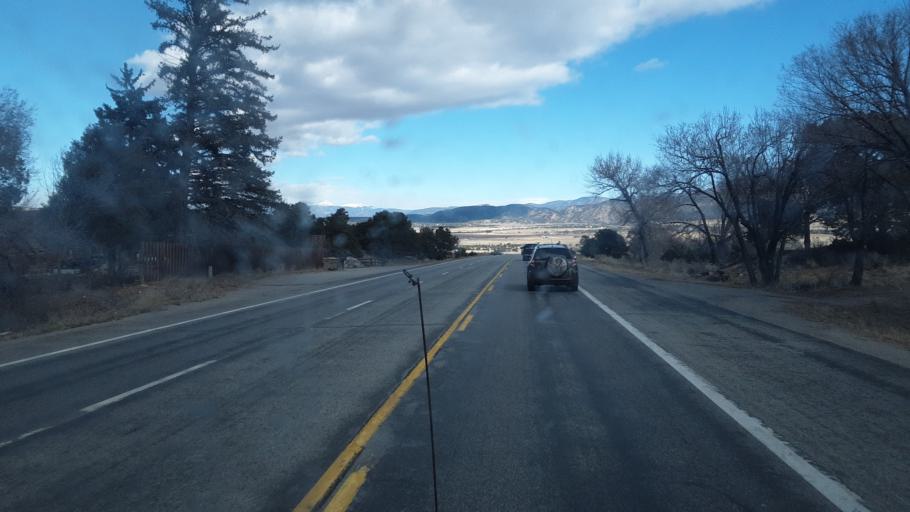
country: US
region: Colorado
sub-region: Chaffee County
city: Salida
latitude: 38.5576
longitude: -106.0825
